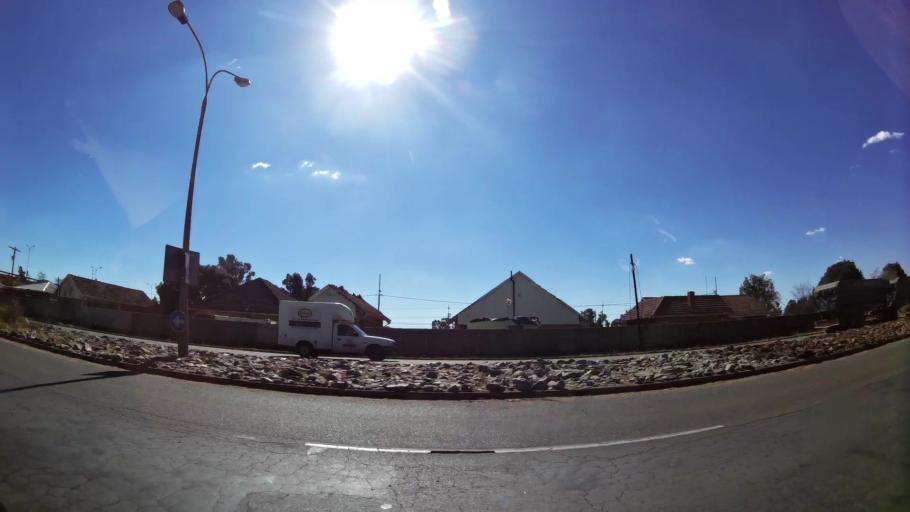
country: ZA
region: Gauteng
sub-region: West Rand District Municipality
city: Carletonville
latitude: -26.3443
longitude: 27.3915
